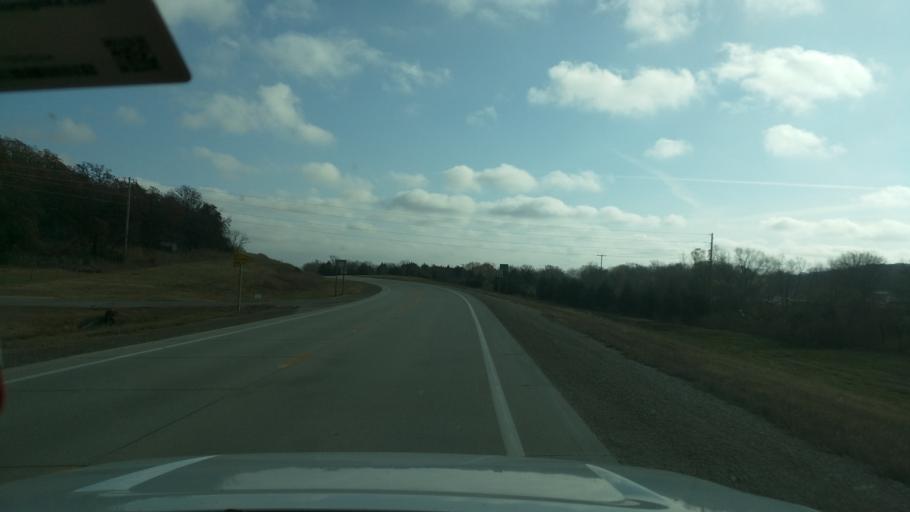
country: US
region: Kansas
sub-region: Montgomery County
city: Caney
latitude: 37.0675
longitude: -96.0224
